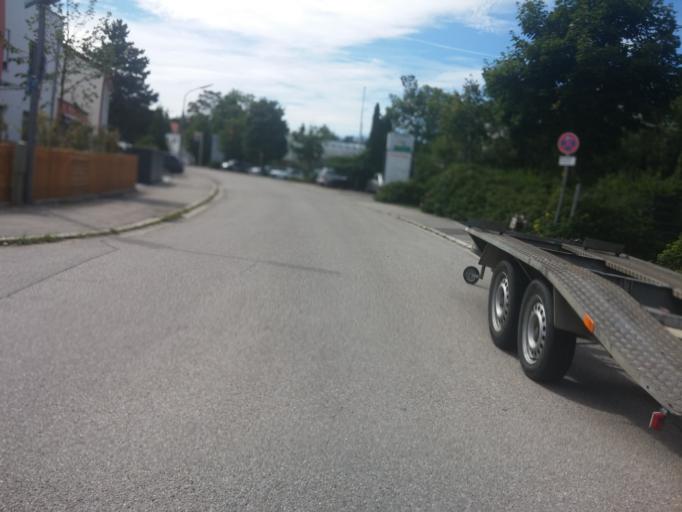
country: DE
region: Bavaria
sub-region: Upper Bavaria
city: Haar
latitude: 48.1183
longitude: 11.6956
